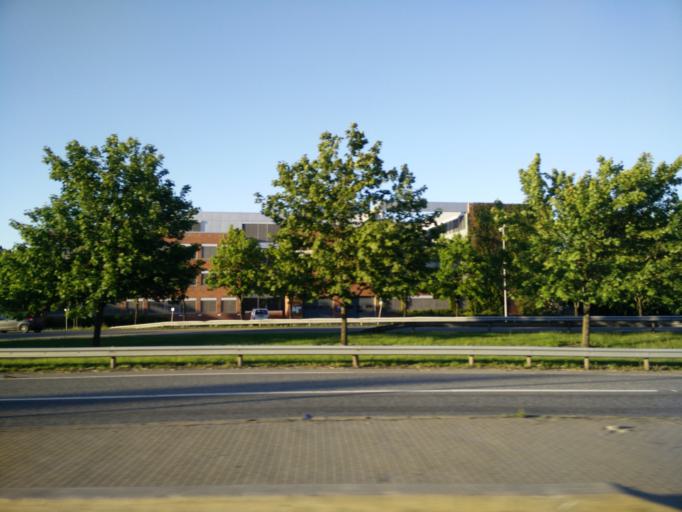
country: NO
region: Akershus
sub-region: Baerum
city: Sandvika
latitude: 59.8922
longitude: 10.5135
